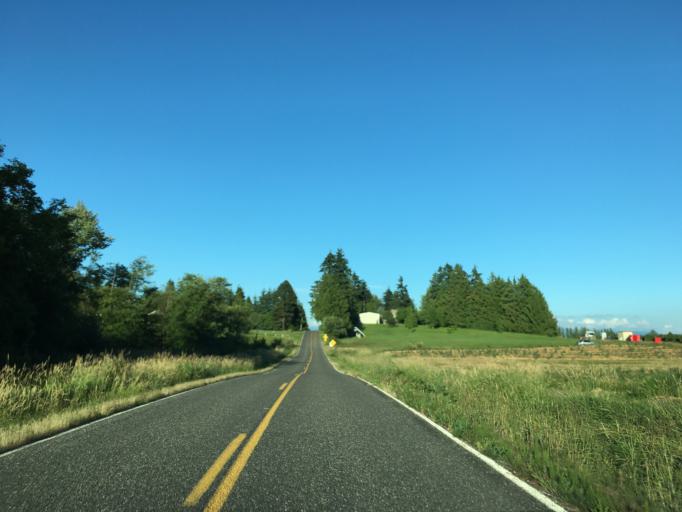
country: US
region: Washington
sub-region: Whatcom County
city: Lynden
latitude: 48.9829
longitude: -122.5223
